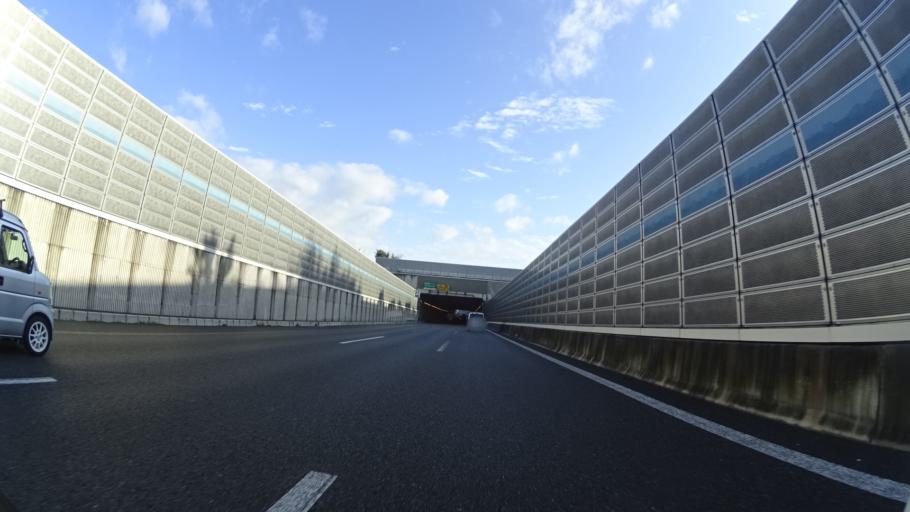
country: JP
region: Kyoto
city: Tanabe
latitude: 34.8084
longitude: 135.7117
